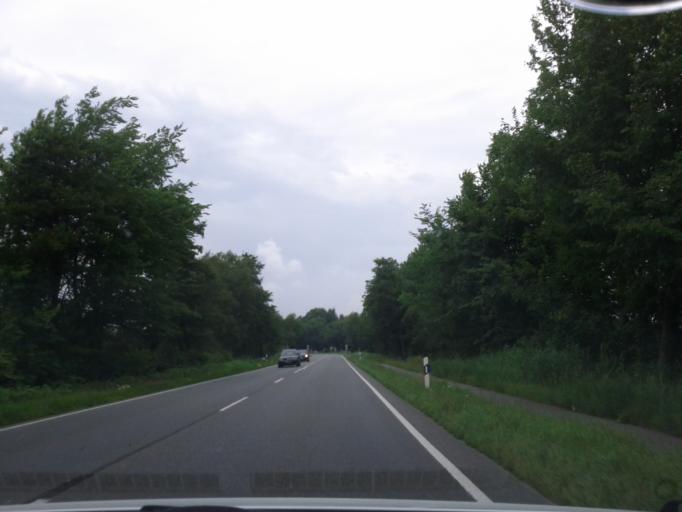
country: DE
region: Lower Saxony
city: Burweg
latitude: 53.6344
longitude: 9.2587
